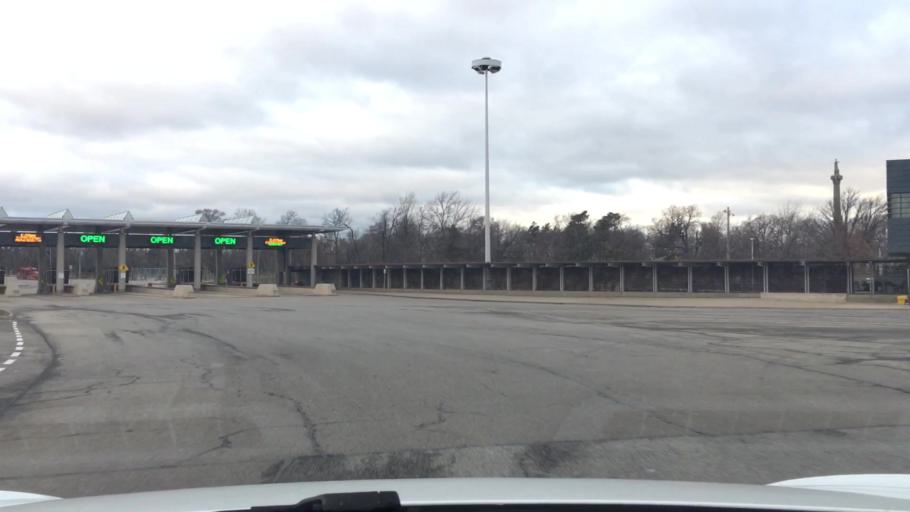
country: US
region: New York
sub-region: Niagara County
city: Lewiston
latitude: 43.1562
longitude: -79.0514
